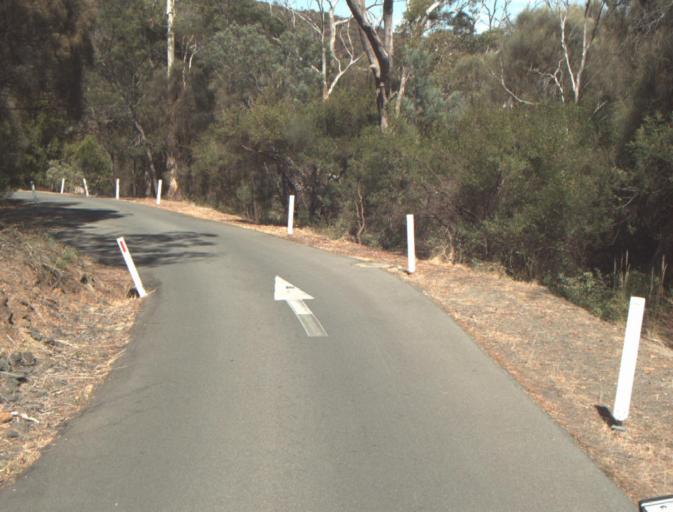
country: AU
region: Tasmania
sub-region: Launceston
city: Summerhill
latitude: -41.4581
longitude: 147.1182
